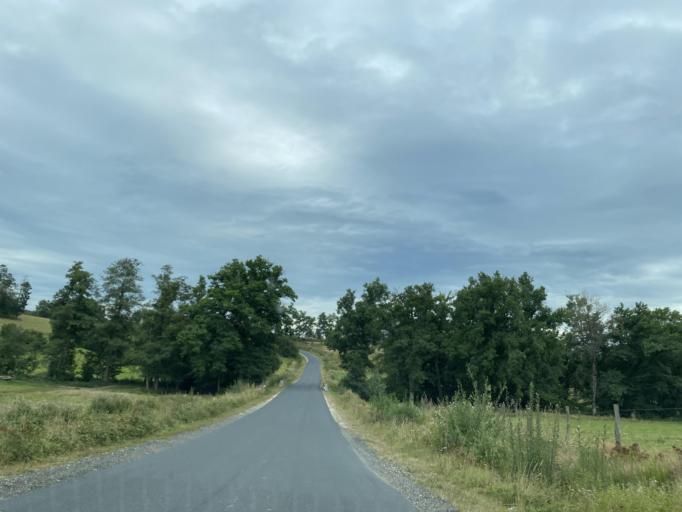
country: FR
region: Auvergne
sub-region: Departement du Puy-de-Dome
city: Ambert
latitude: 45.5222
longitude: 3.7413
